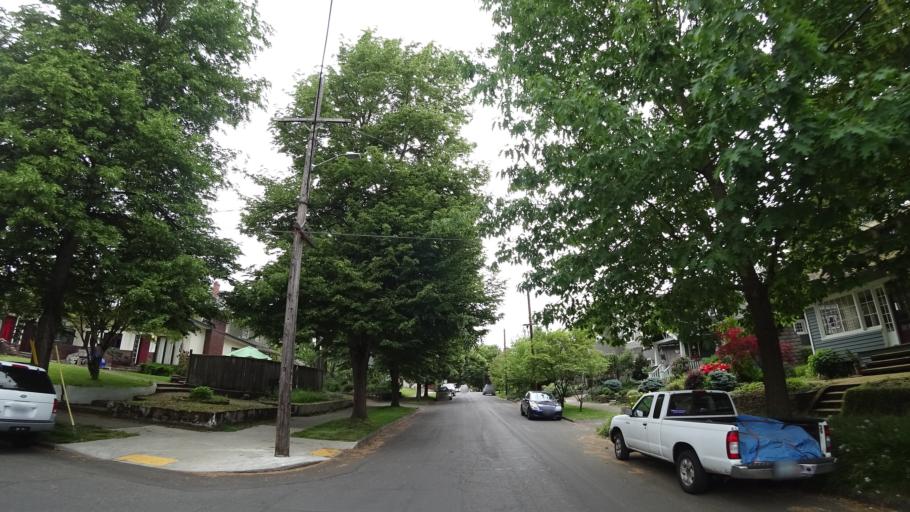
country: US
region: Oregon
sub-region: Multnomah County
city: Portland
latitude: 45.5020
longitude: -122.6326
